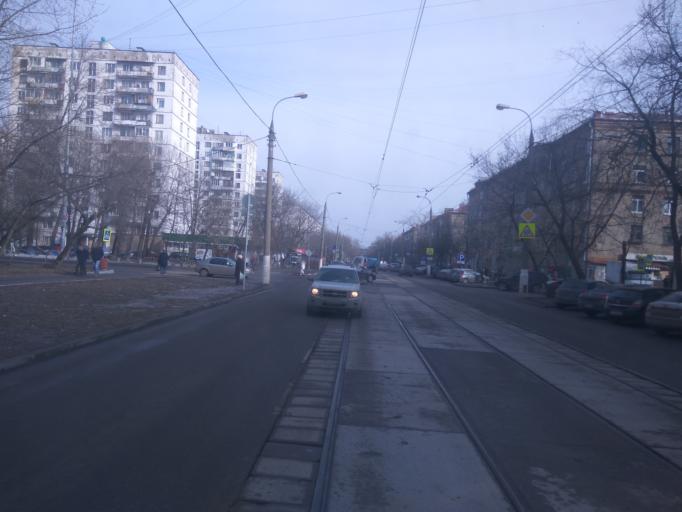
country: RU
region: Moscow
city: Kolomenskoye
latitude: 55.6837
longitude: 37.6847
